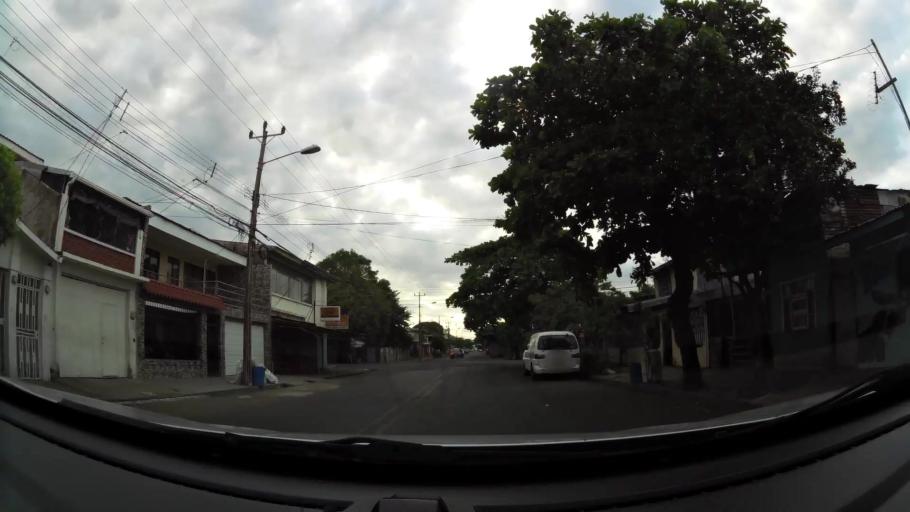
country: CR
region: Puntarenas
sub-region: Canton Central de Puntarenas
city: Puntarenas
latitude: 9.9765
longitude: -84.8423
